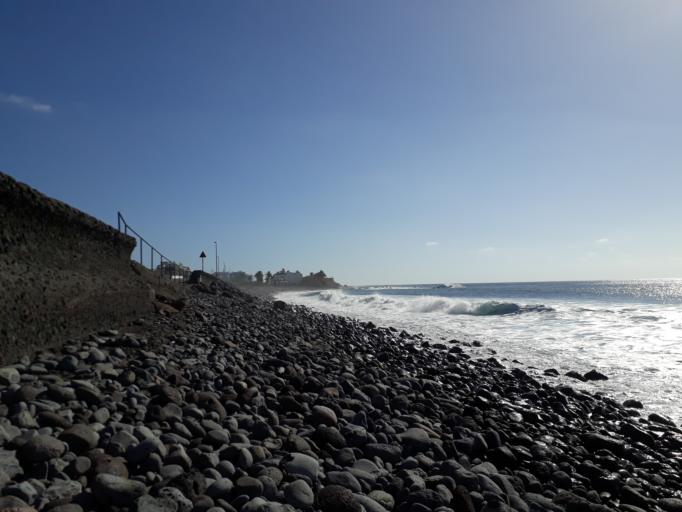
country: ES
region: Canary Islands
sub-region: Provincia de Santa Cruz de Tenerife
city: Alajero
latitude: 28.0919
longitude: -17.3403
